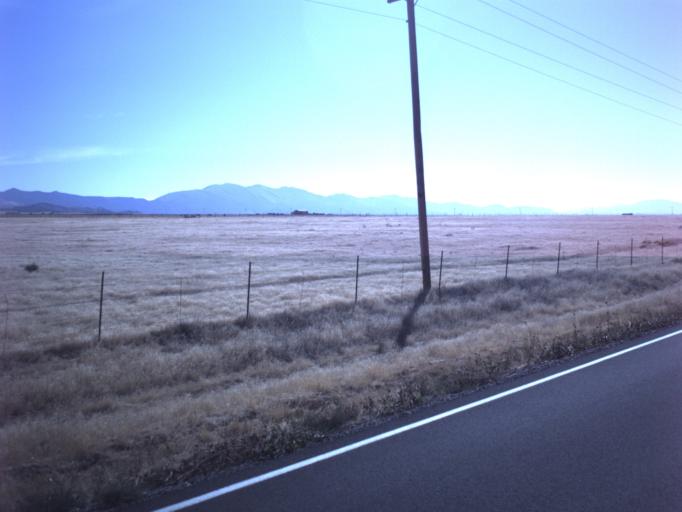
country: US
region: Utah
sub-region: Tooele County
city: Grantsville
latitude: 40.4074
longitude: -112.7483
